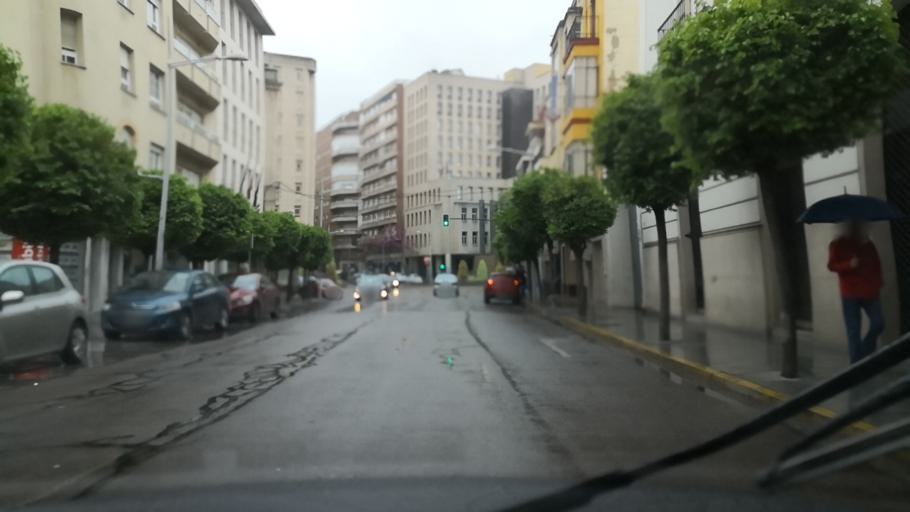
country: ES
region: Extremadura
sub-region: Provincia de Badajoz
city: Badajoz
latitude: 38.8759
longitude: -6.9723
